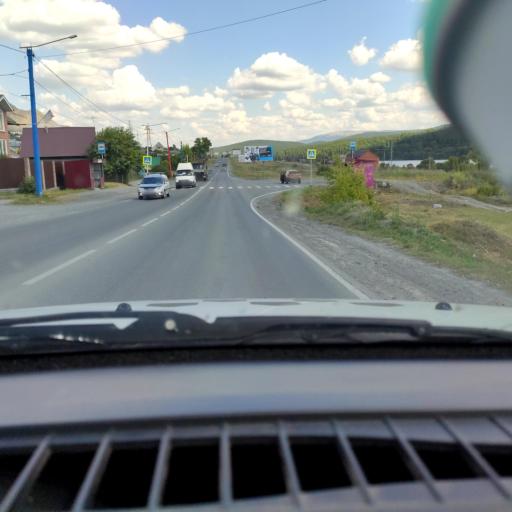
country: RU
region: Chelyabinsk
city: Satka
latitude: 55.0335
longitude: 58.9871
